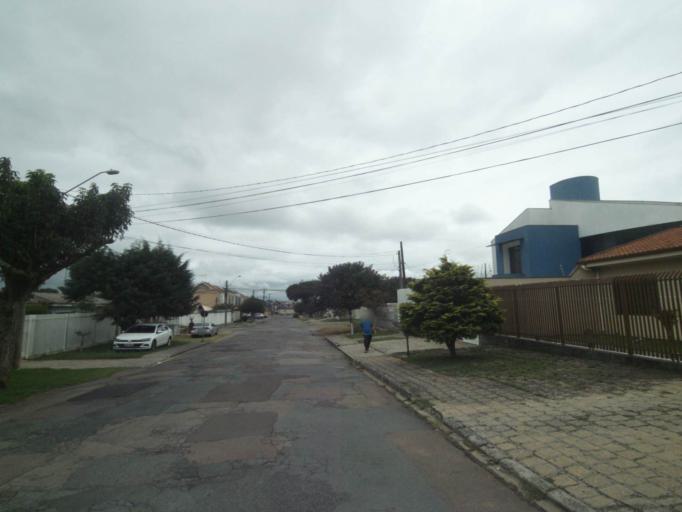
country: BR
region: Parana
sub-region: Curitiba
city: Curitiba
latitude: -25.4890
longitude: -49.2801
